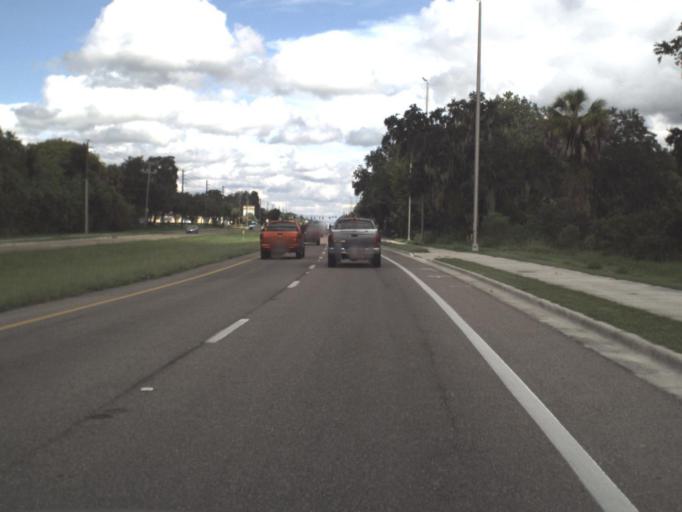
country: US
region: Florida
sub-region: Manatee County
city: Ellenton
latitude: 27.5326
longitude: -82.4968
